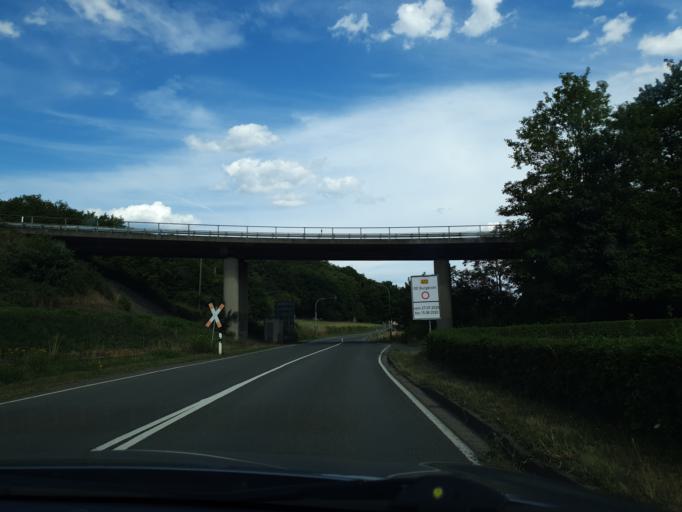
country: DE
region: Rheinland-Pfalz
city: Niederzissen
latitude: 50.4629
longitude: 7.2423
